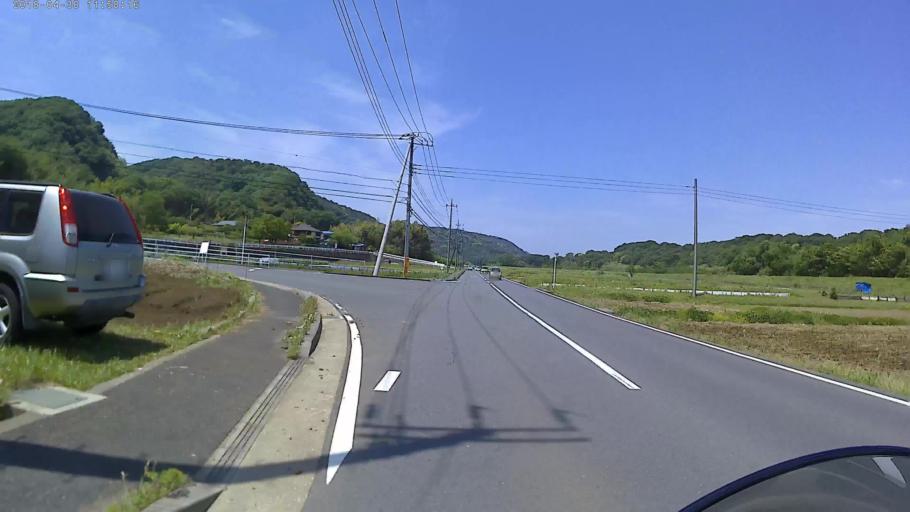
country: JP
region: Kanagawa
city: Zama
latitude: 35.5004
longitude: 139.3373
